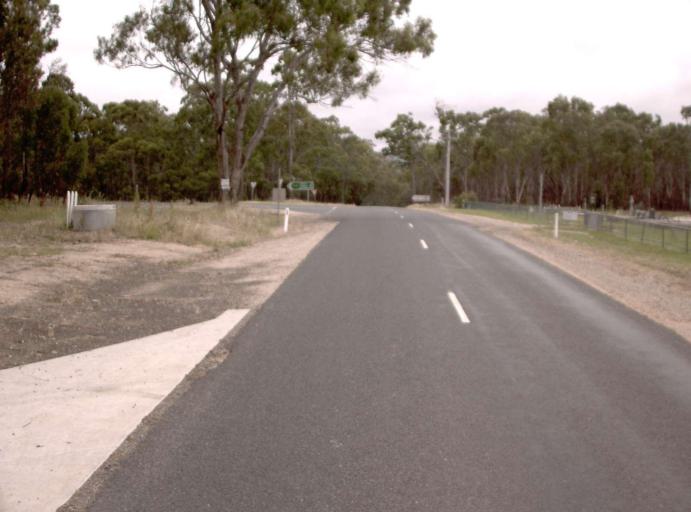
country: AU
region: Victoria
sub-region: Wellington
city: Heyfield
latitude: -37.9055
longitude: 146.7556
